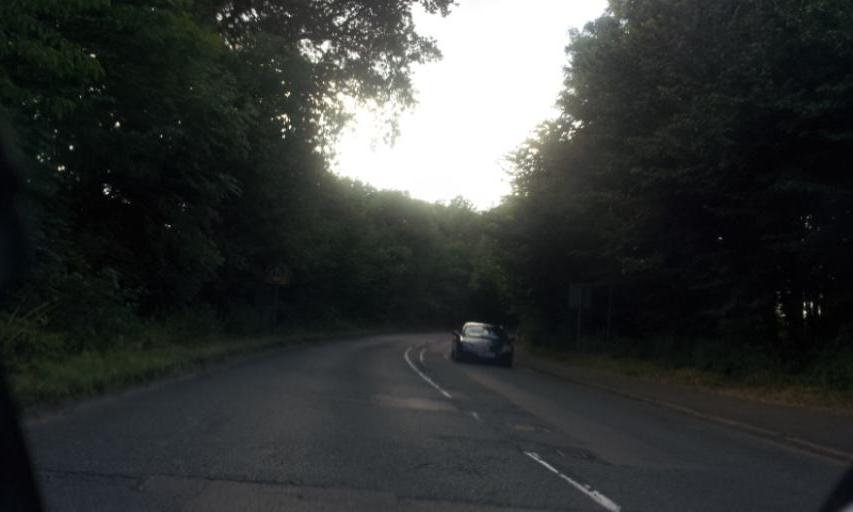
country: GB
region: England
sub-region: Kent
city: Boxley
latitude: 51.2901
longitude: 0.5266
